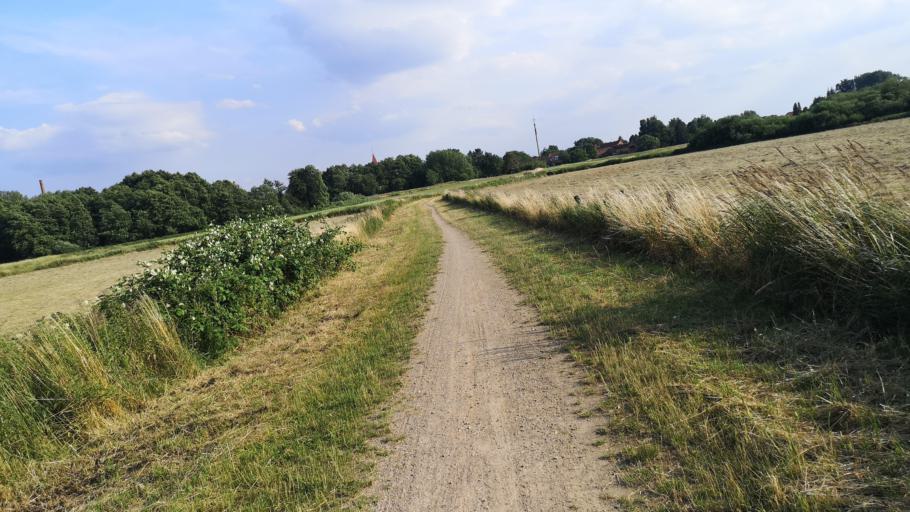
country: DE
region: Lower Saxony
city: Dahlenburg
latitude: 53.1935
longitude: 10.7400
